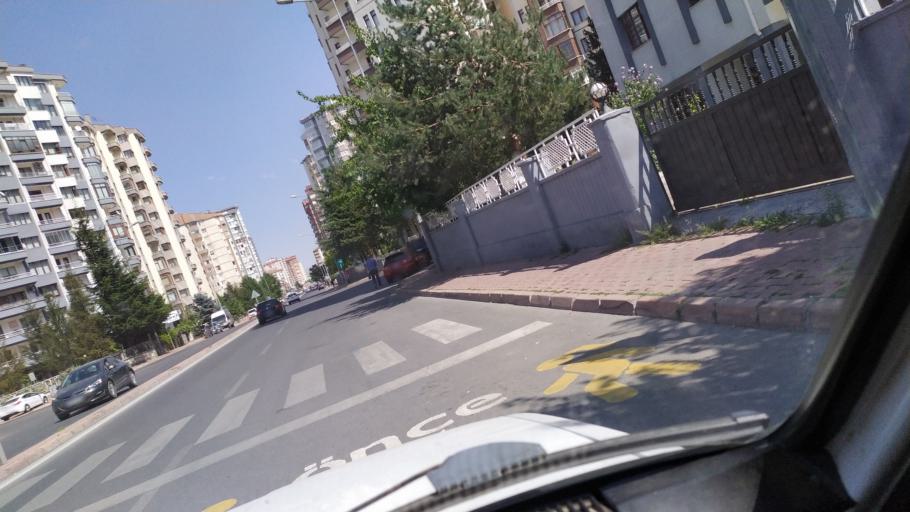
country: TR
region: Kayseri
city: Kayseri
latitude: 38.7287
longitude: 35.5214
